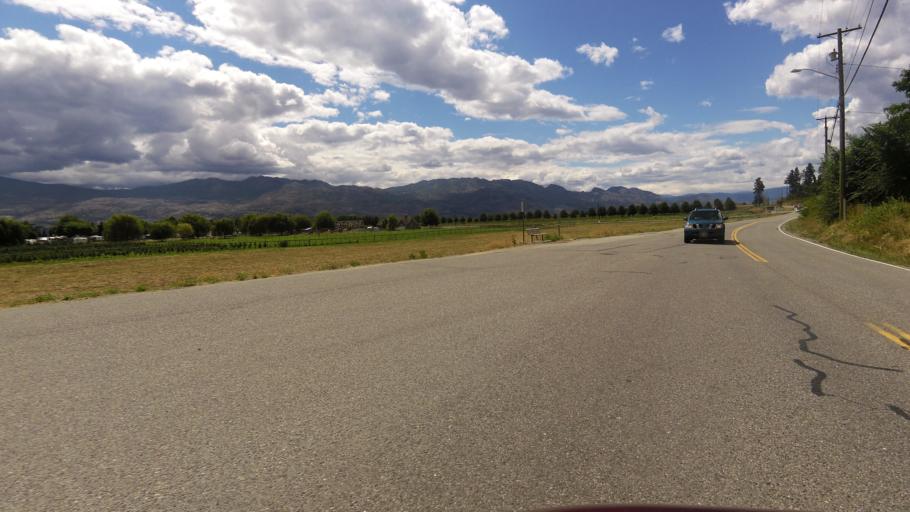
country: CA
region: British Columbia
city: West Kelowna
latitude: 49.8350
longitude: -119.5792
